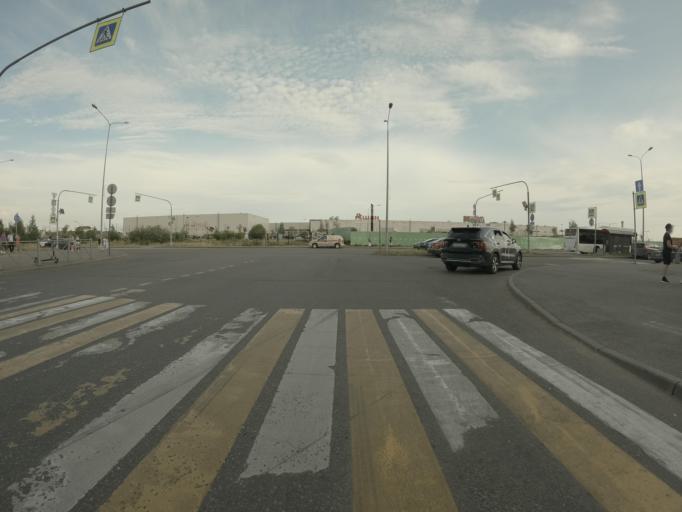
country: RU
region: Leningrad
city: Rybatskoye
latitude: 59.8973
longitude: 30.5128
